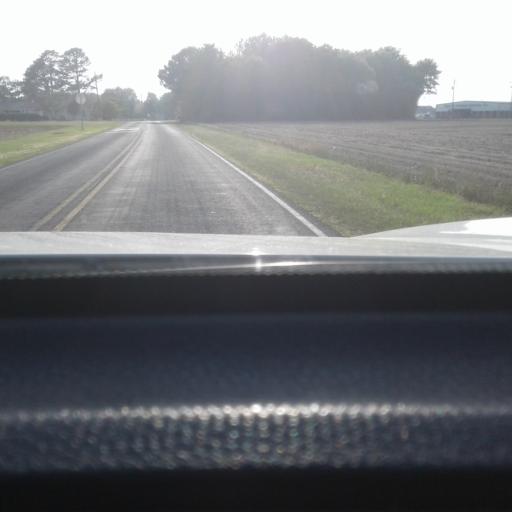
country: US
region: North Carolina
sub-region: Harnett County
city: Dunn
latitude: 35.3355
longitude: -78.5878
